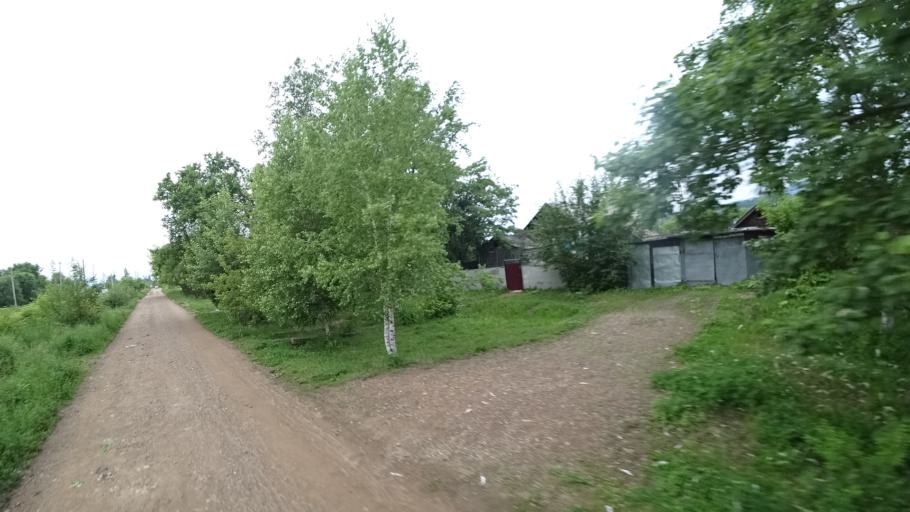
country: RU
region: Primorskiy
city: Novosysoyevka
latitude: 44.2319
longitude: 133.3657
